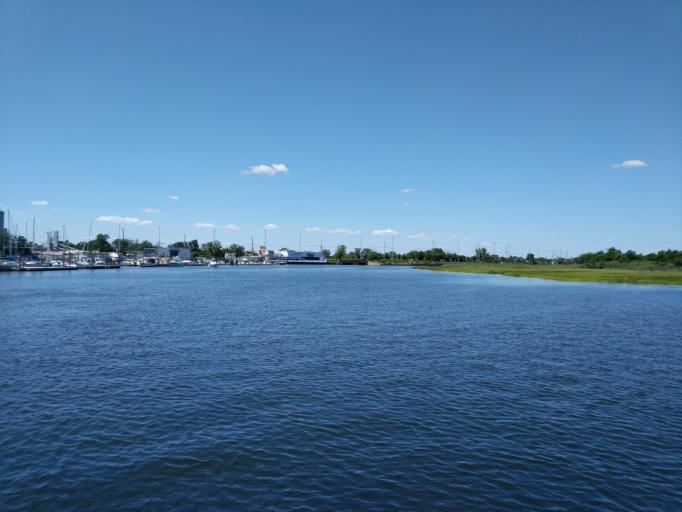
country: US
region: New York
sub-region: Nassau County
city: Barnum Island
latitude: 40.6141
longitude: -73.6398
